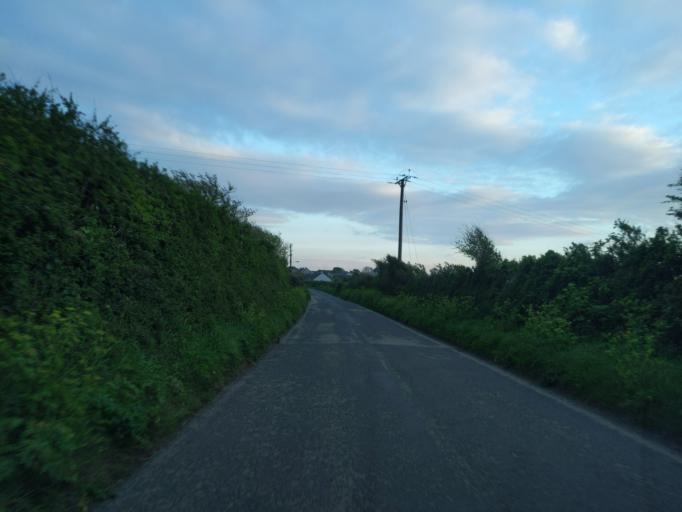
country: GB
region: England
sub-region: Cornwall
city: Polzeath
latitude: 50.5632
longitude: -4.8719
